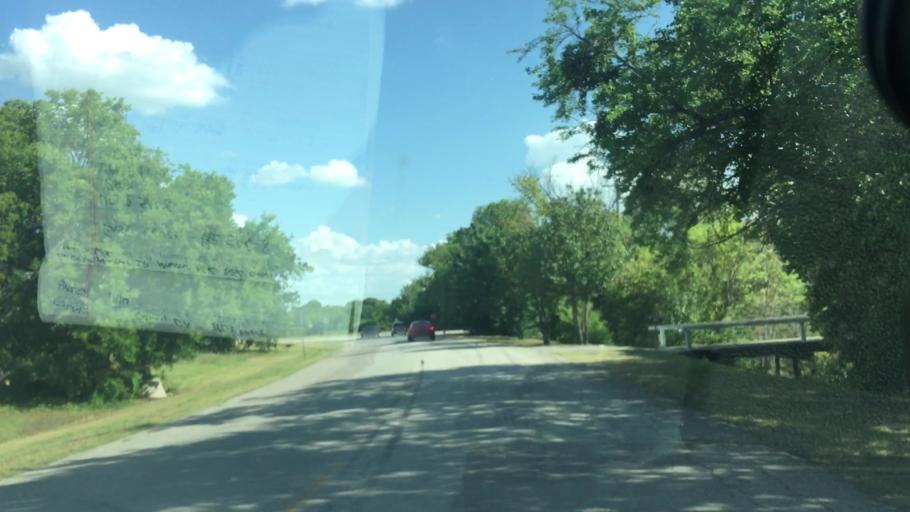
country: US
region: Texas
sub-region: Dallas County
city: Lancaster
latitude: 32.6052
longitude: -96.7535
